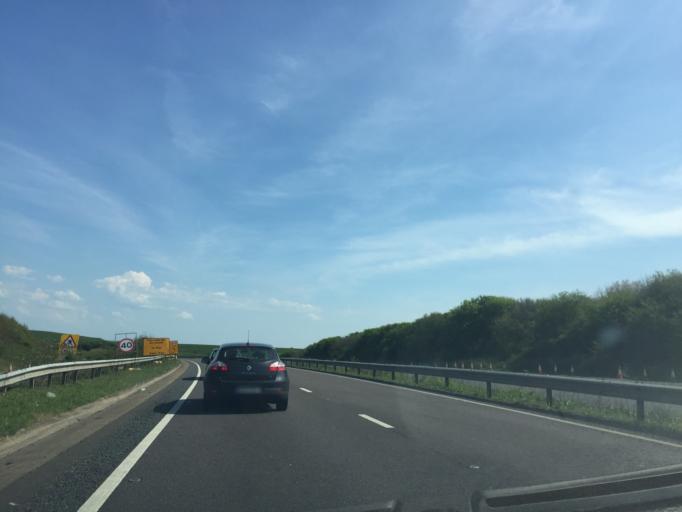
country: GB
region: England
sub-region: Kent
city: Folkestone
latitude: 51.1064
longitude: 1.2351
